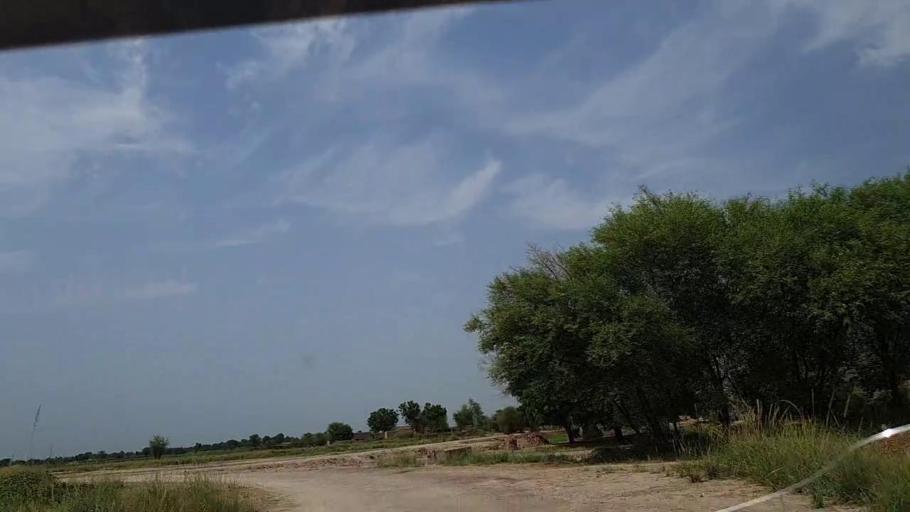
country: PK
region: Sindh
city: Tharu Shah
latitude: 26.8944
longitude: 68.0798
